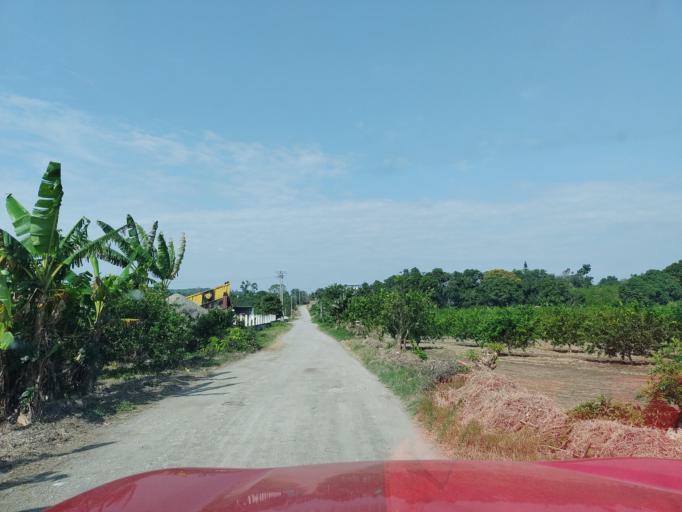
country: MX
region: Puebla
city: Espinal
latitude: 20.2721
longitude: -97.3278
